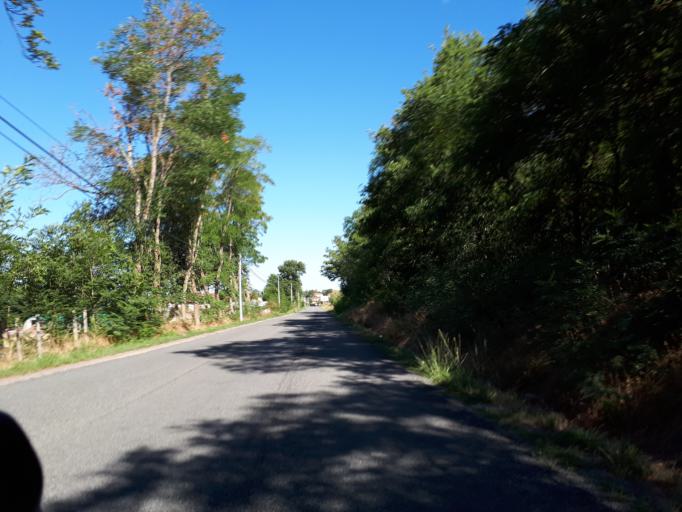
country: FR
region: Rhone-Alpes
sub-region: Departement de la Loire
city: Civens
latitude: 45.7748
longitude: 4.2575
